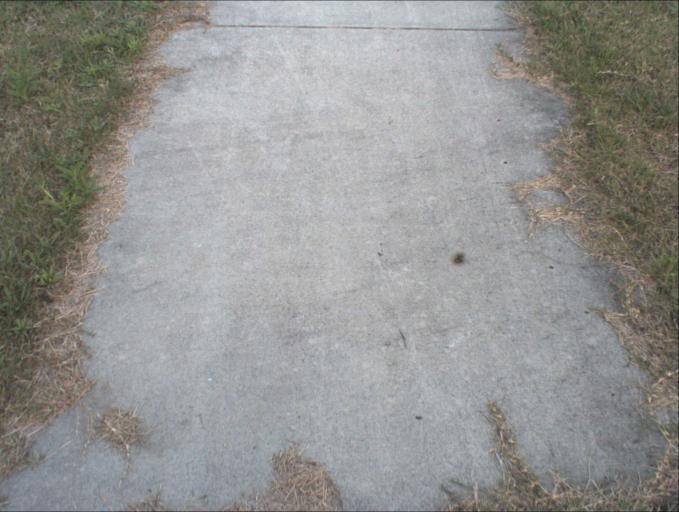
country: AU
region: Queensland
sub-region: Logan
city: North Maclean
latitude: -27.7992
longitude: 152.9560
